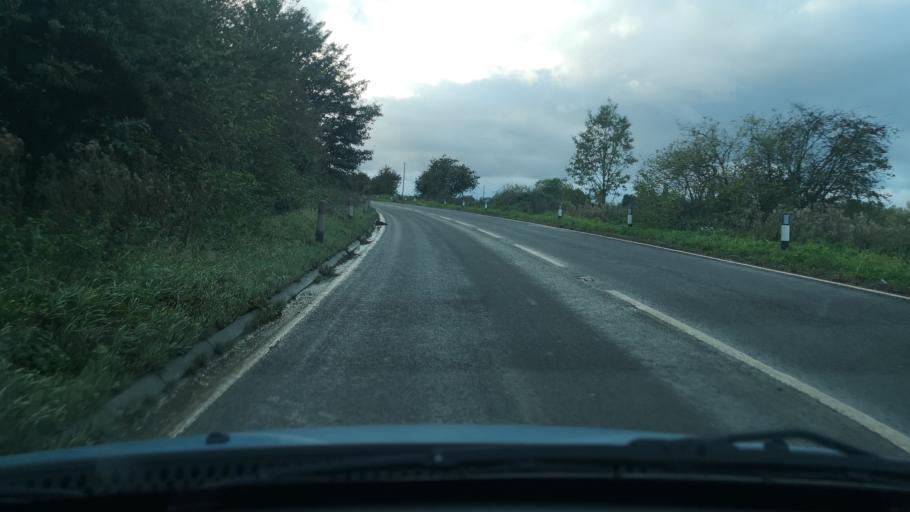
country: GB
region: England
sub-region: North Lincolnshire
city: Crowle
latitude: 53.5877
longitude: -0.8266
